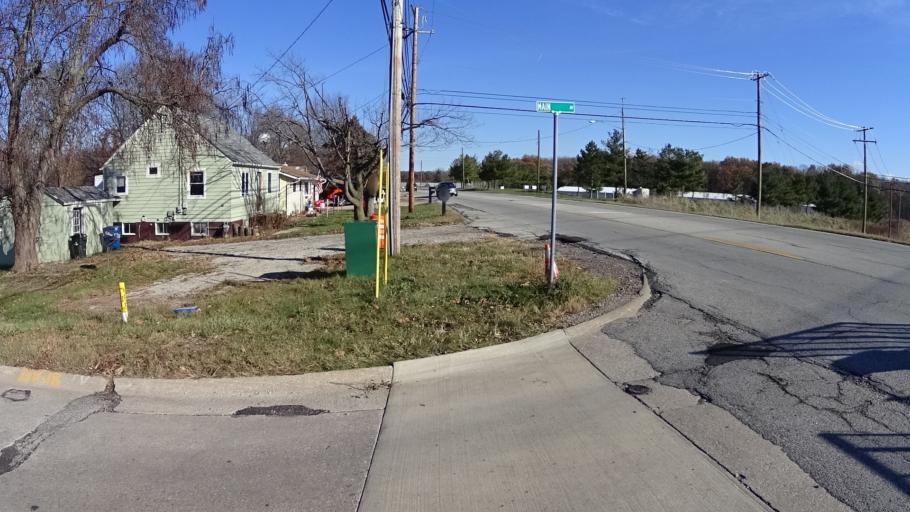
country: US
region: Ohio
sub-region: Lorain County
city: North Ridgeville
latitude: 41.4023
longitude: -81.9878
